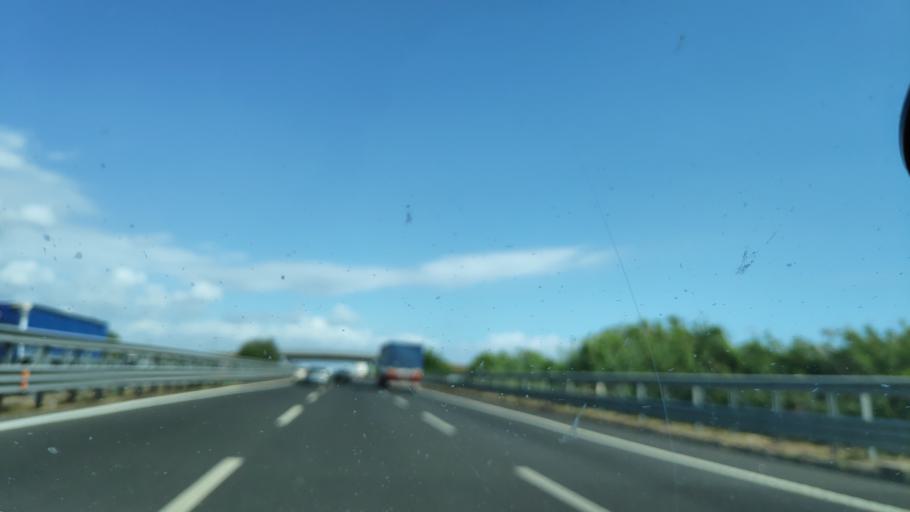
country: IT
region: Campania
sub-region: Provincia di Salerno
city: Pontecagnano
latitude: 40.6472
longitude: 14.8856
